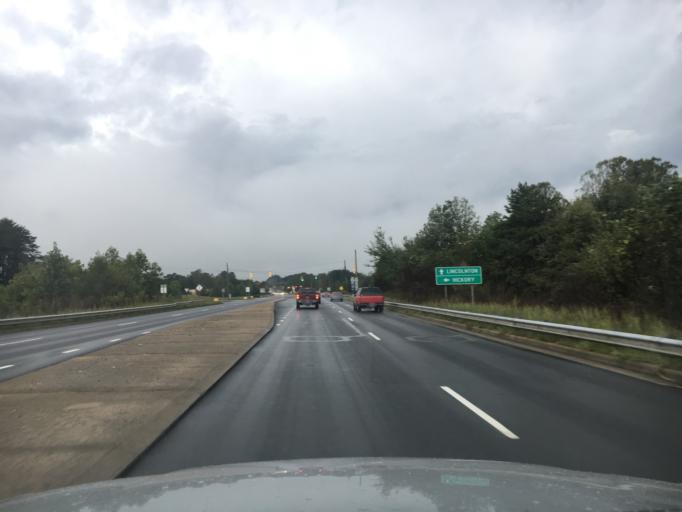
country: US
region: North Carolina
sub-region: Catawba County
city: Mountain View
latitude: 35.6958
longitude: -81.3493
